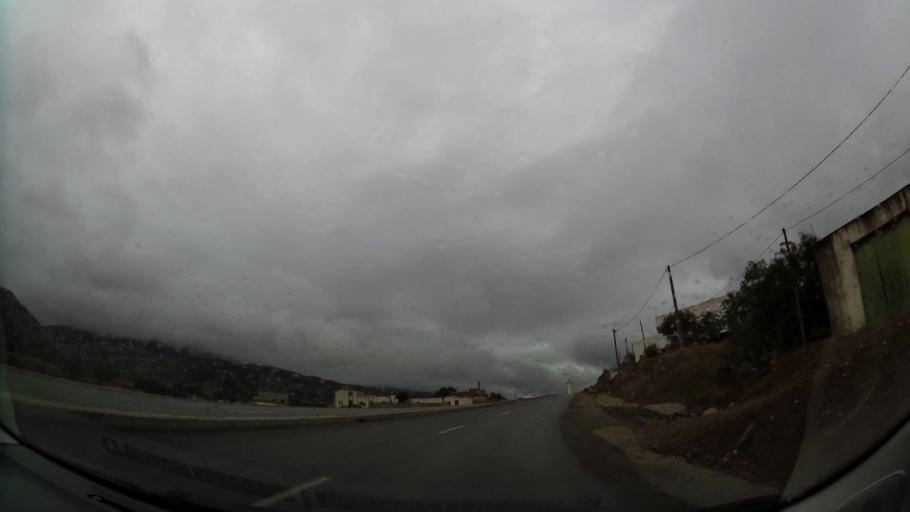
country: MA
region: Taza-Al Hoceima-Taounate
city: Imzourene
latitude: 34.9871
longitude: -3.8106
